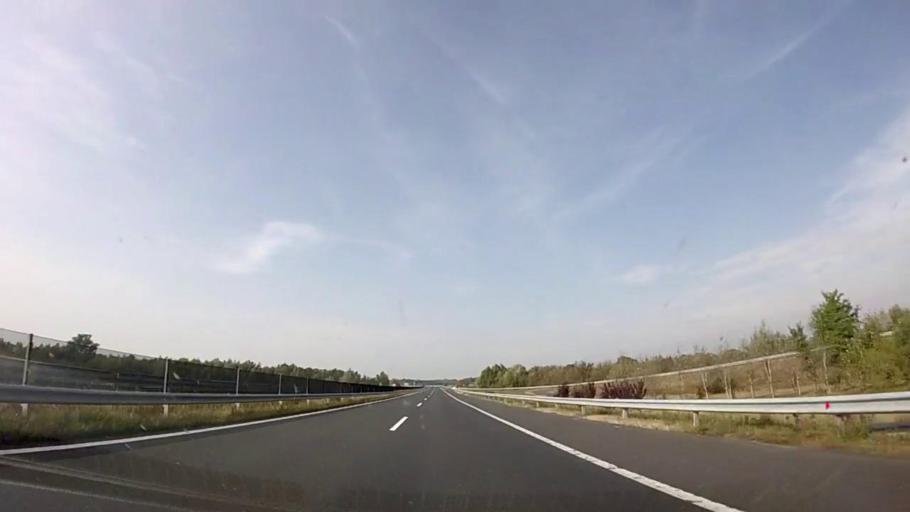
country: HU
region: Zala
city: Nagykanizsa
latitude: 46.4775
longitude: 16.9731
